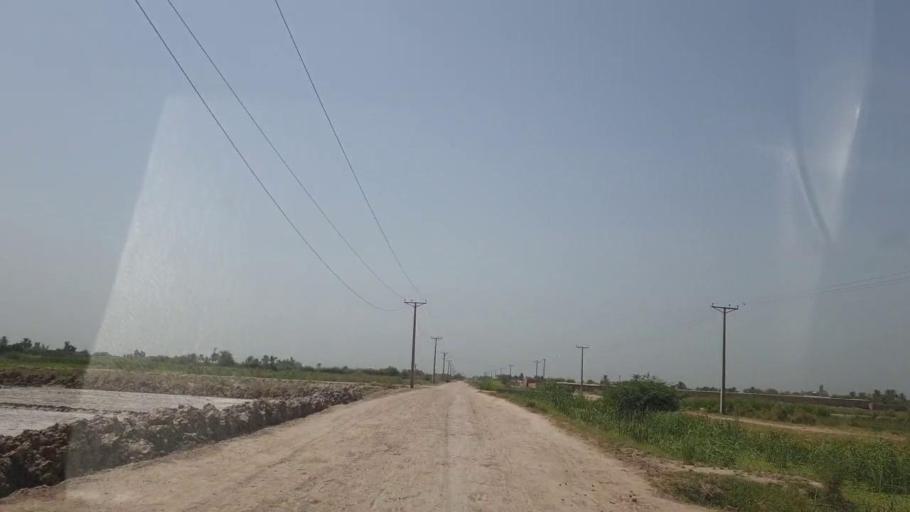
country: PK
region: Sindh
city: Ranipur
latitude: 27.3025
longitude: 68.5452
